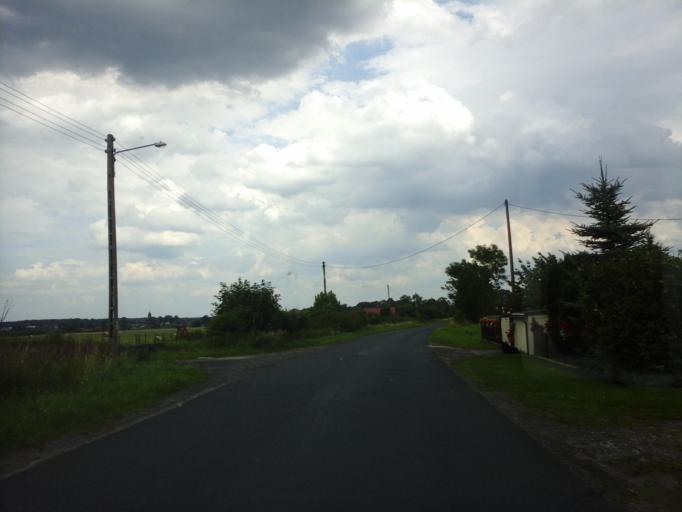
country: PL
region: West Pomeranian Voivodeship
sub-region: Powiat choszczenski
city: Bierzwnik
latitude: 53.0469
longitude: 15.7289
